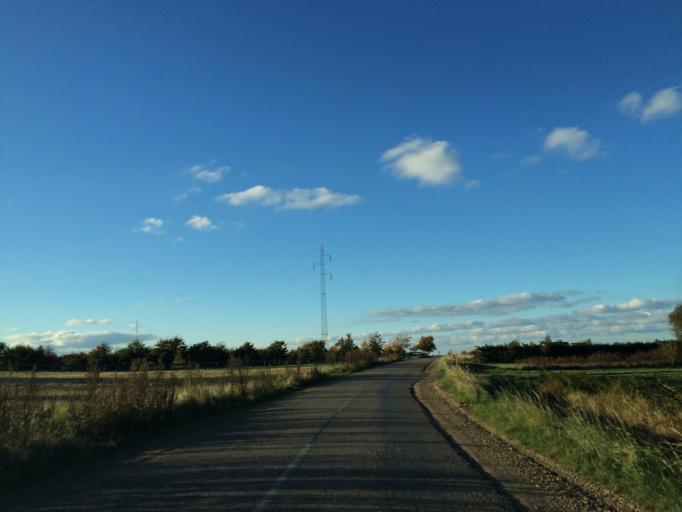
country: DK
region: Central Jutland
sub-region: Silkeborg Kommune
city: Svejbaek
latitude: 56.1430
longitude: 9.7082
